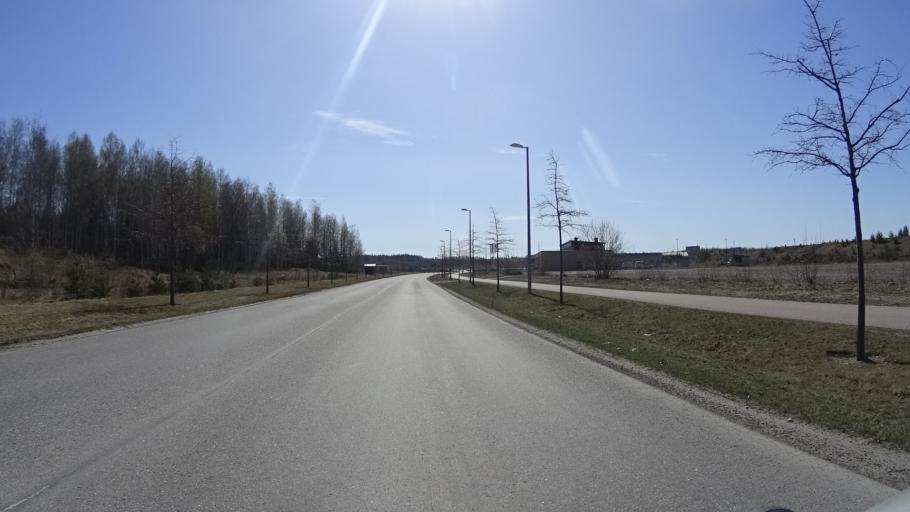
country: SE
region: Soedermanland
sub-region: Katrineholms Kommun
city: Katrineholm
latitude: 59.0039
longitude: 16.2329
